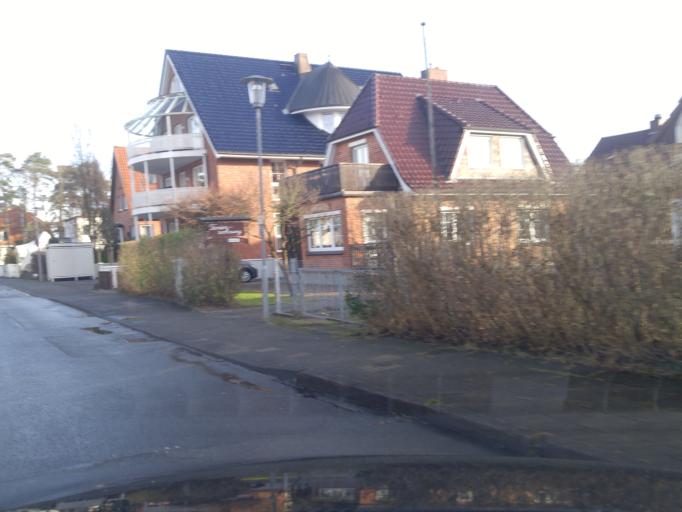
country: DE
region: Schleswig-Holstein
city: Timmendorfer Strand
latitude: 53.9957
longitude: 10.7846
